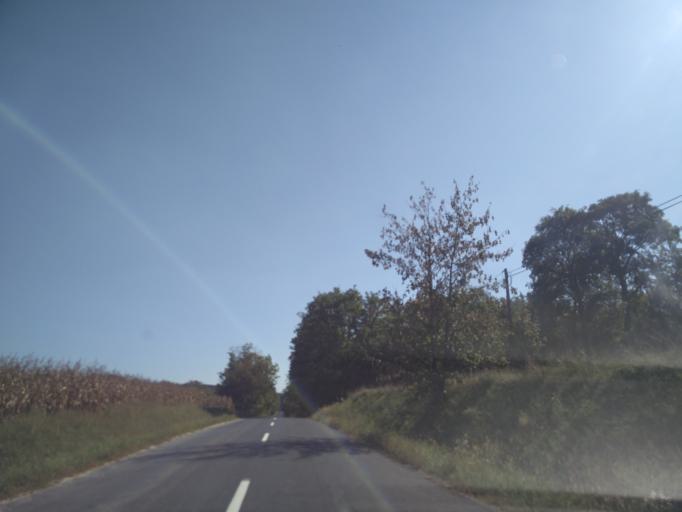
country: HU
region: Fejer
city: Lovasbereny
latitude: 47.2917
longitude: 18.5721
